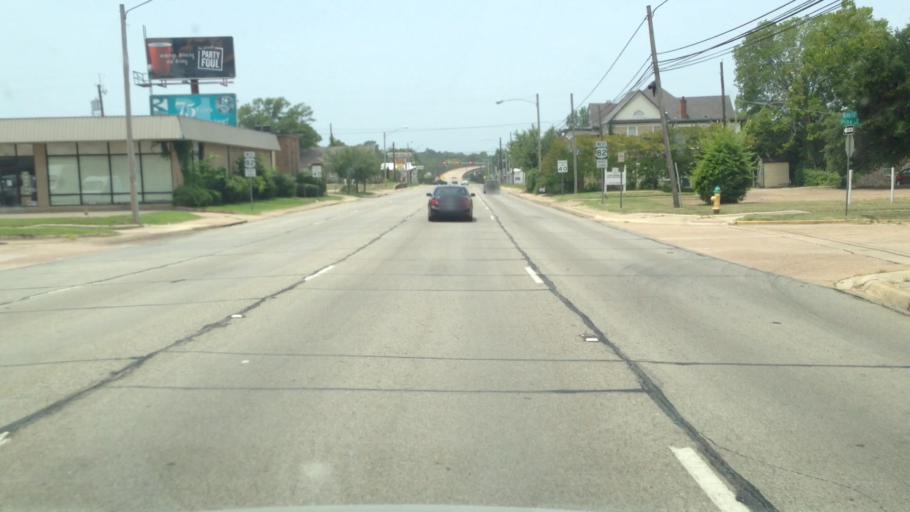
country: US
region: Texas
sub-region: Bowie County
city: Texarkana
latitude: 33.4271
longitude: -94.0461
